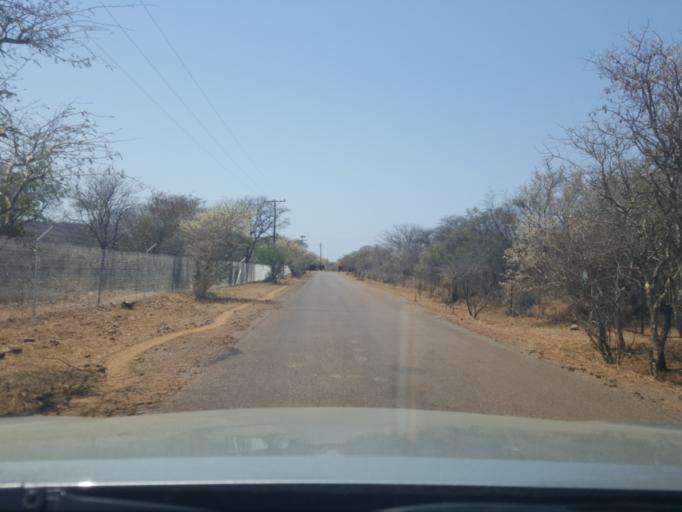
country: BW
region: South East
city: Ramotswa
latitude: -24.7632
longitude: 25.8436
